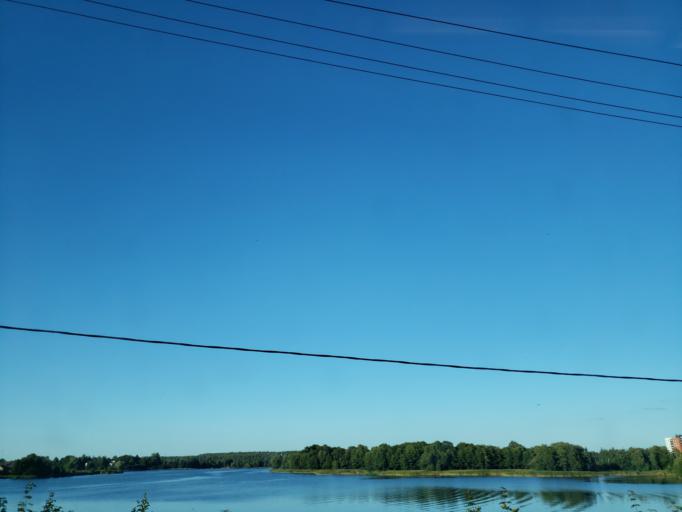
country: RU
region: Leningrad
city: Vyborg
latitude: 60.7174
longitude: 28.7433
